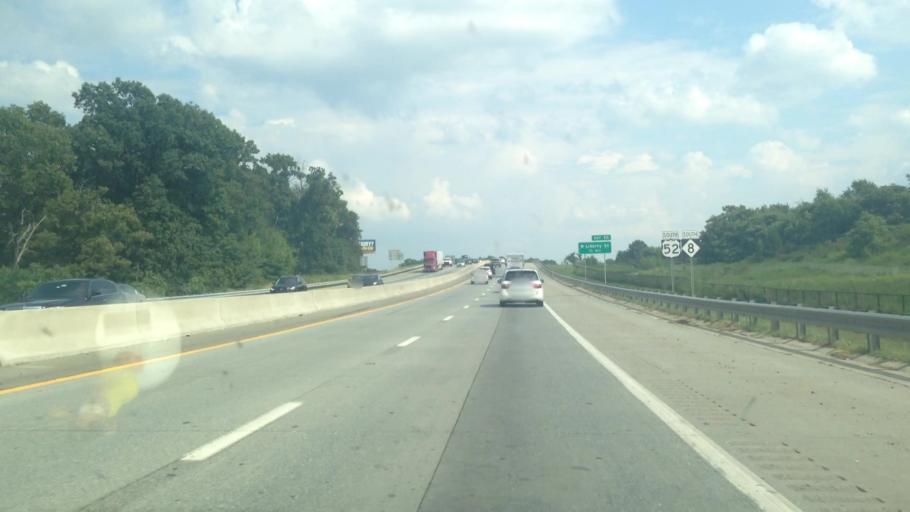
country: US
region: North Carolina
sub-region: Forsyth County
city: Winston-Salem
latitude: 36.1315
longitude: -80.2370
